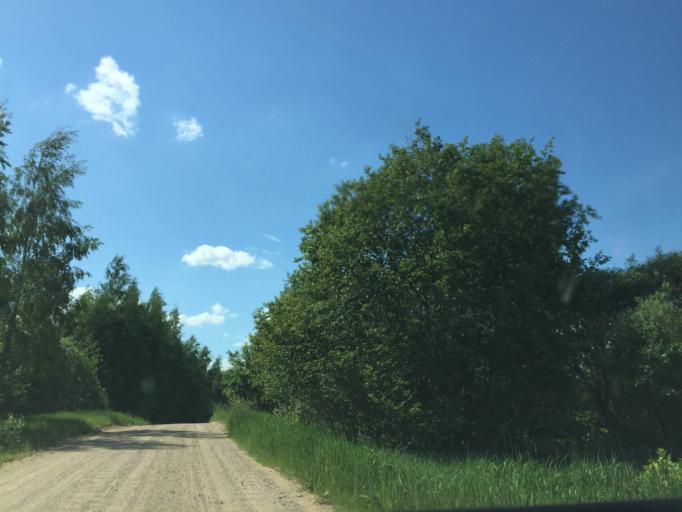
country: LV
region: Priekuli
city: Priekuli
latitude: 57.2535
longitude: 25.3966
